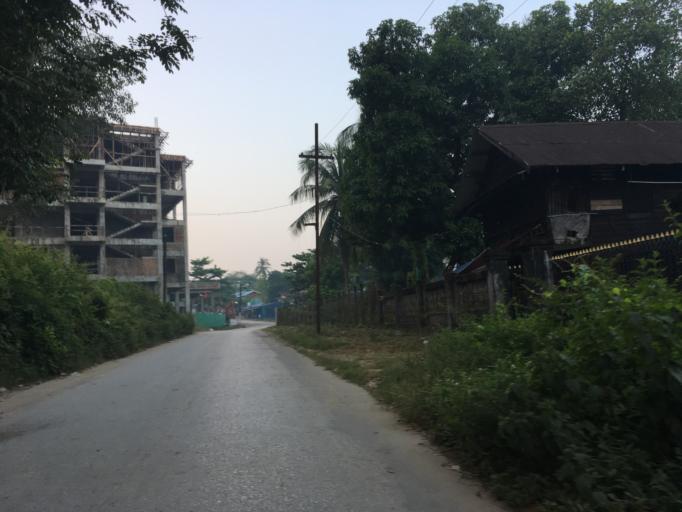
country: MM
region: Mon
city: Mawlamyine
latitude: 16.4825
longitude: 97.6266
